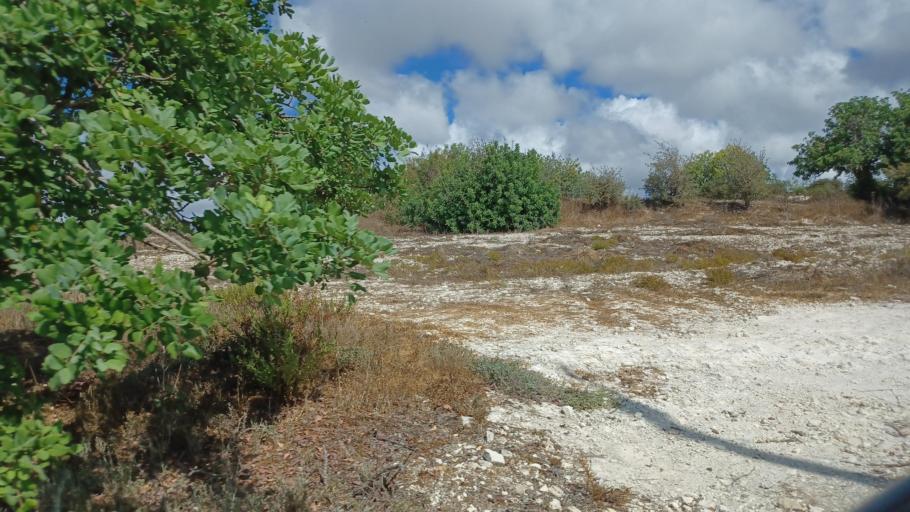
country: CY
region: Pafos
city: Tala
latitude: 34.8555
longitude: 32.4354
